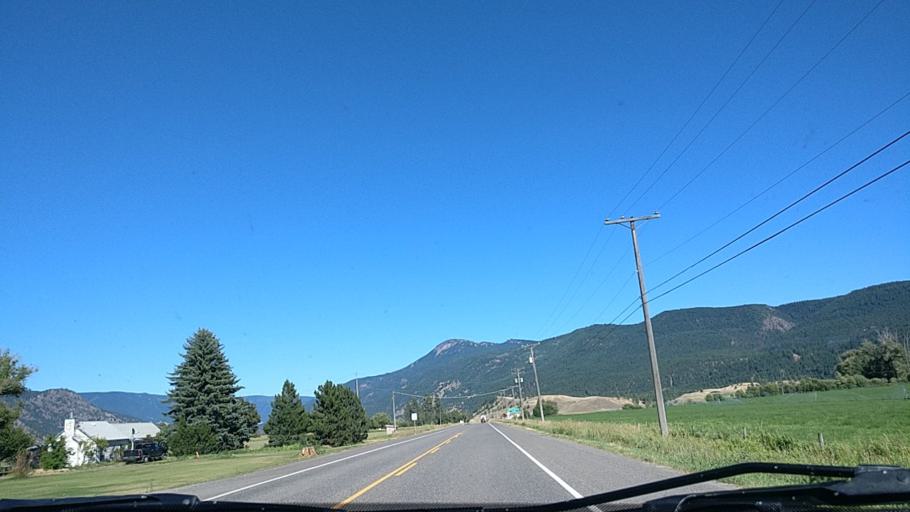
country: CA
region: British Columbia
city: Chase
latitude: 50.4612
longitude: -119.7318
